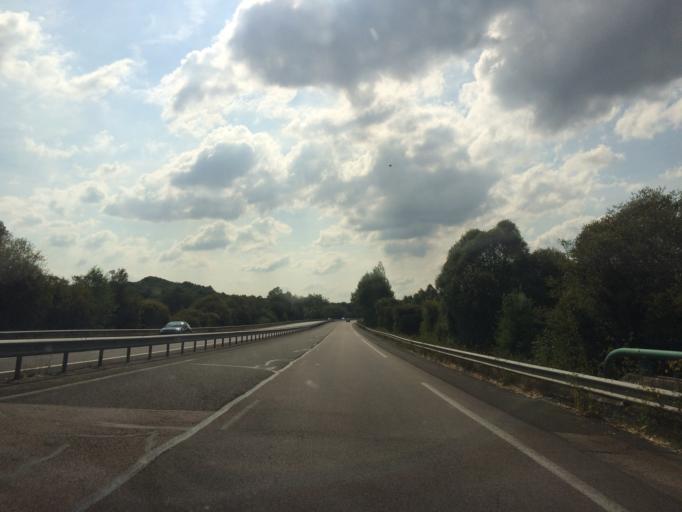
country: FR
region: Lower Normandy
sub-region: Departement de l'Orne
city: Mortagne-au-Perche
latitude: 48.5120
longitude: 0.4211
